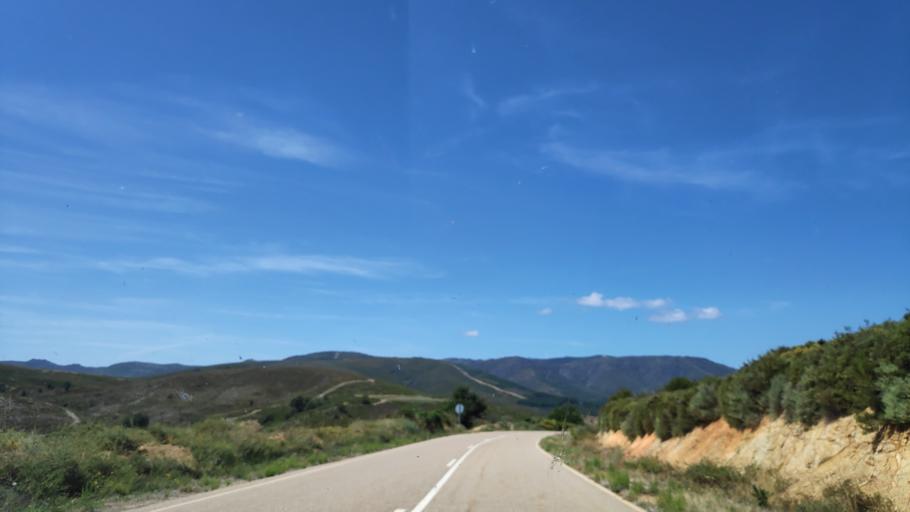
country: ES
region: Castille and Leon
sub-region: Provincia de Zamora
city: Requejo
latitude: 42.0196
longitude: -6.6962
